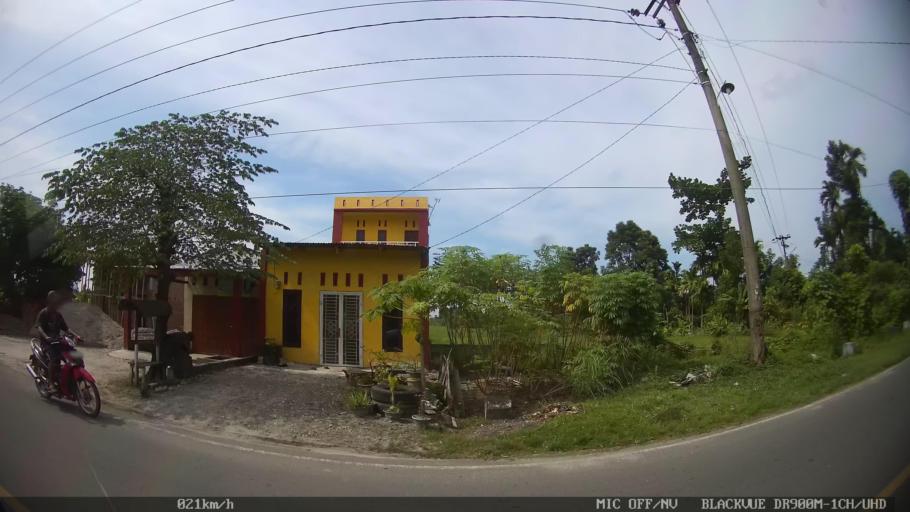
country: ID
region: North Sumatra
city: Percut
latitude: 3.6110
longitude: 98.8307
